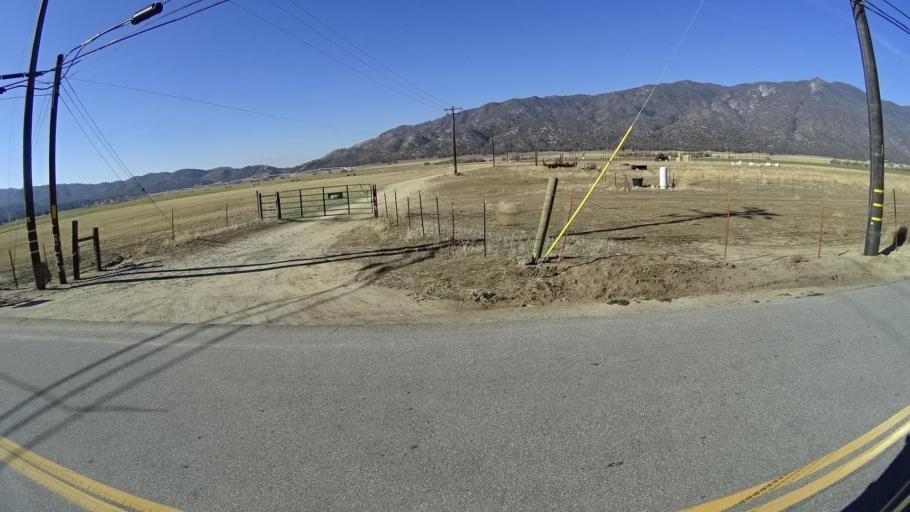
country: US
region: California
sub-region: Kern County
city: Bodfish
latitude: 35.4014
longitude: -118.5227
